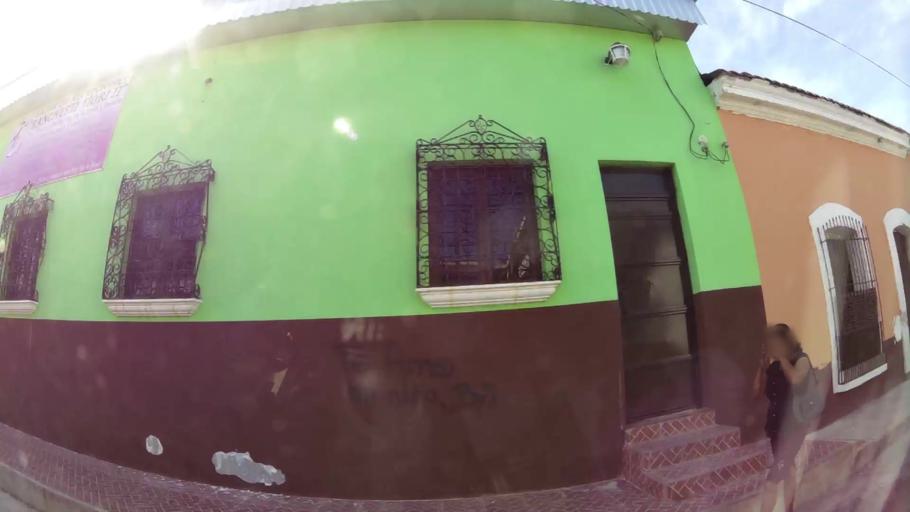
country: SV
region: Santa Ana
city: Chalchuapa
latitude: 13.9826
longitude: -89.6803
